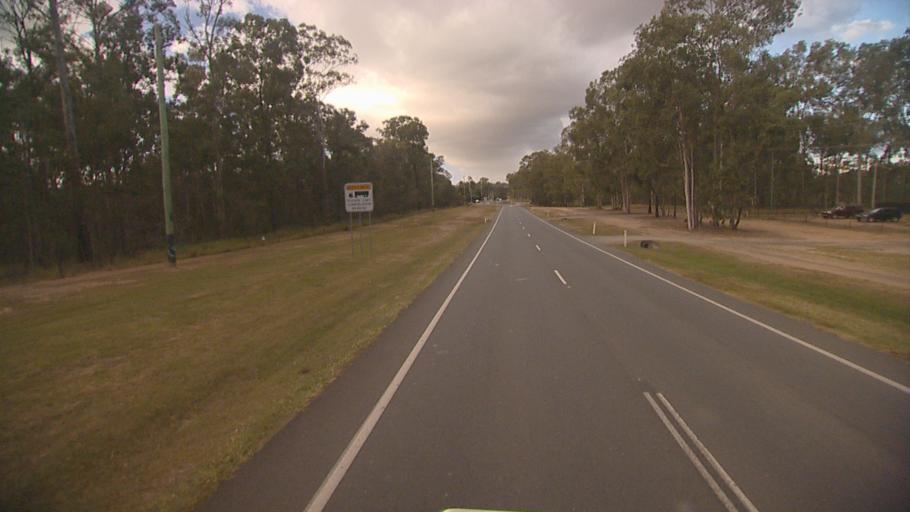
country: AU
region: Queensland
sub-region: Logan
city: Park Ridge South
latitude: -27.7081
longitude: 153.0006
